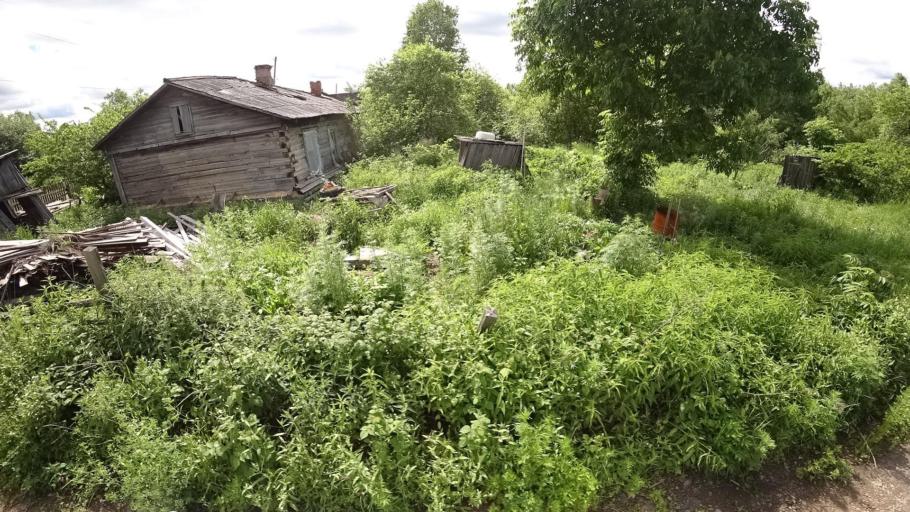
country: RU
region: Khabarovsk Krai
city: Litovko
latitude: 49.3686
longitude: 135.1700
